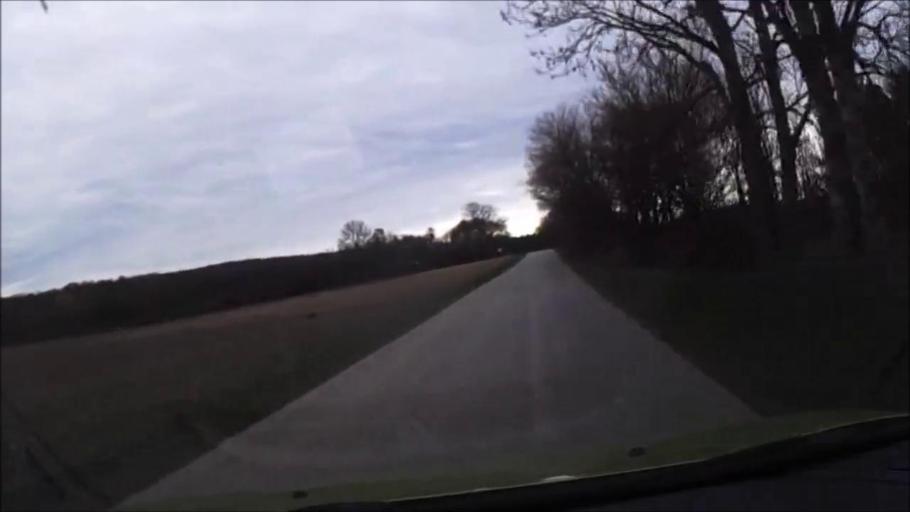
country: AT
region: Burgenland
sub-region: Eisenstadt-Umgebung
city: Loretto
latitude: 47.9090
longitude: 16.5149
